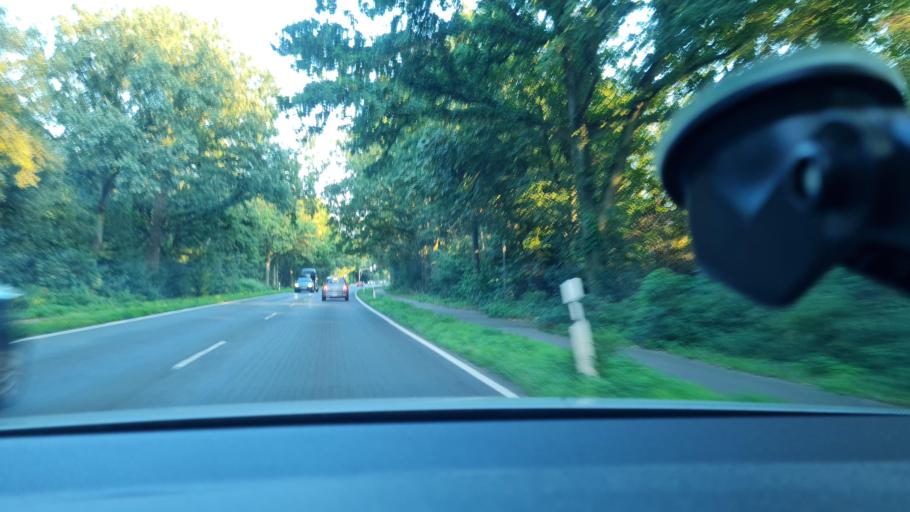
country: DE
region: North Rhine-Westphalia
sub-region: Regierungsbezirk Dusseldorf
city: Dinslaken
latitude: 51.5562
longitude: 6.7750
